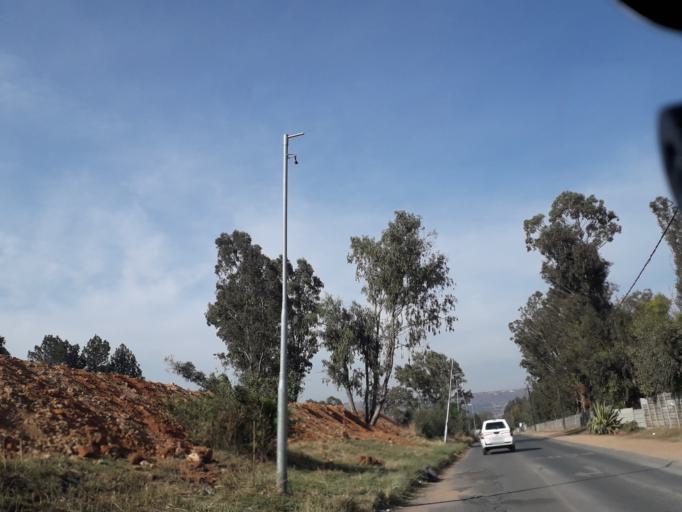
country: ZA
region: Gauteng
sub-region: West Rand District Municipality
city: Muldersdriseloop
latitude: -26.0649
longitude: 27.9038
